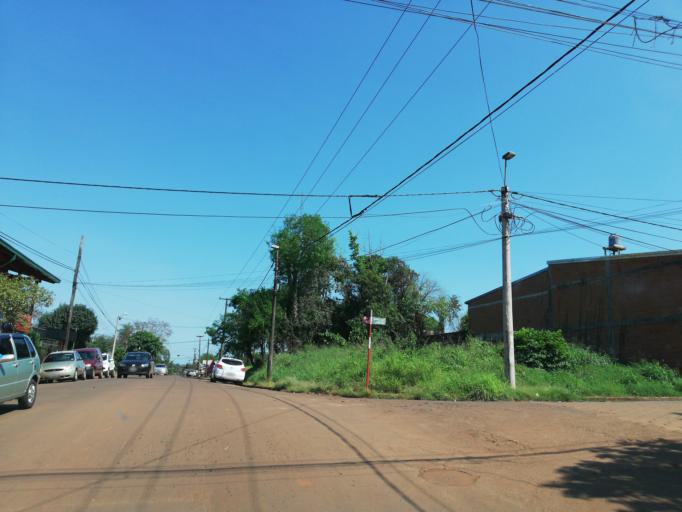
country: AR
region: Misiones
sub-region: Departamento de Eldorado
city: Eldorado
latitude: -26.4110
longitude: -54.6098
